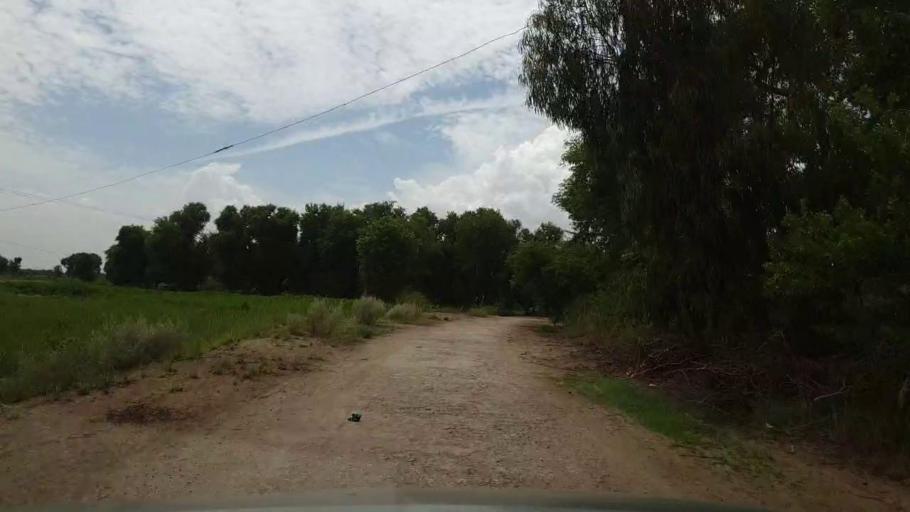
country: PK
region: Sindh
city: Bozdar
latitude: 27.0560
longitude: 68.9669
